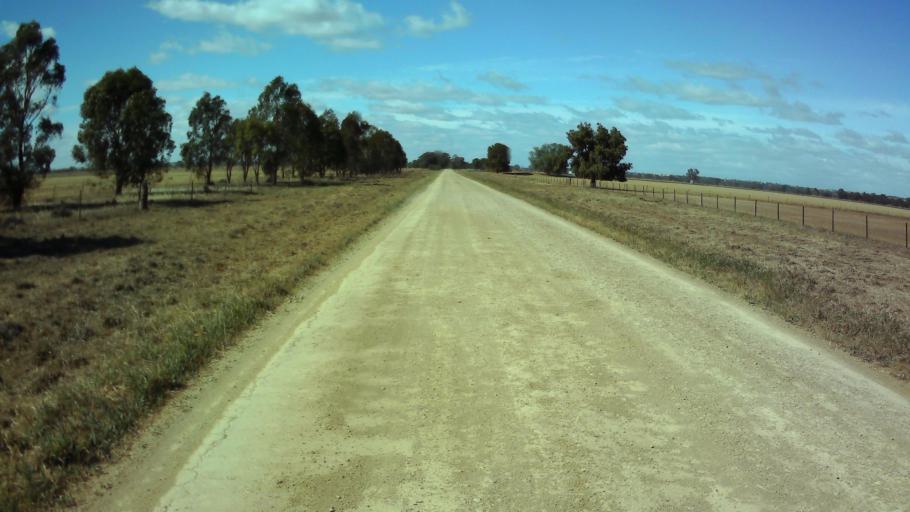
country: AU
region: New South Wales
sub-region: Weddin
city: Grenfell
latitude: -34.0195
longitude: 148.3193
